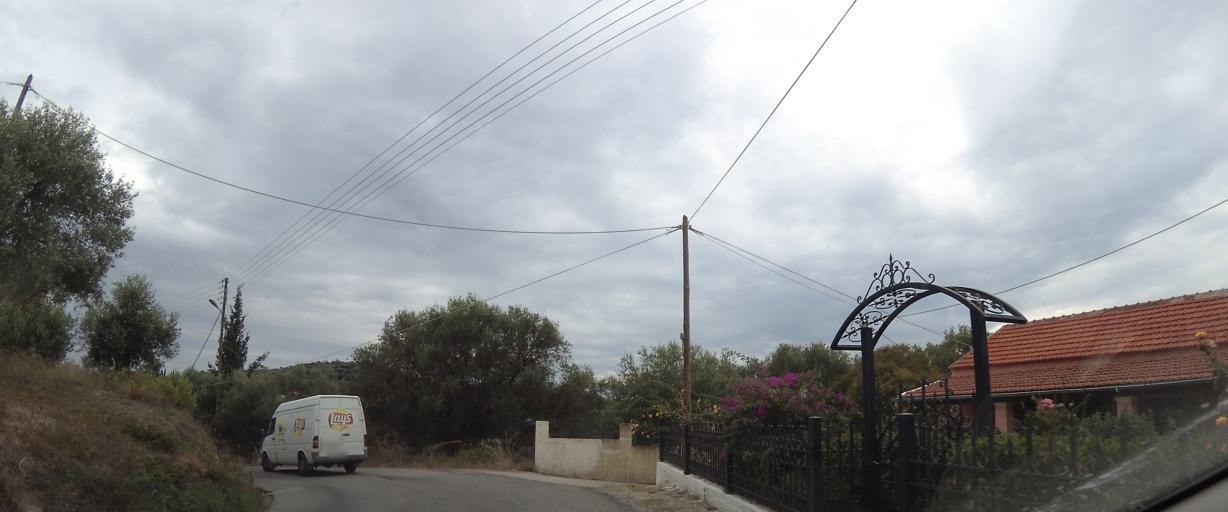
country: GR
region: Ionian Islands
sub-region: Nomos Kerkyras
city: Agios Georgis
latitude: 39.7395
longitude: 19.6742
